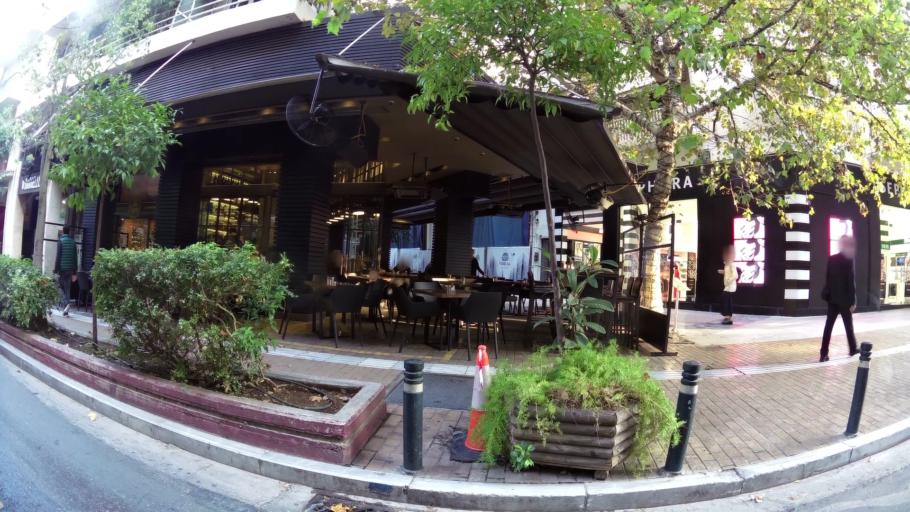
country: GR
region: Attica
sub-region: Nomarchia Athinas
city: Vyronas
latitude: 37.9771
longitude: 23.7397
